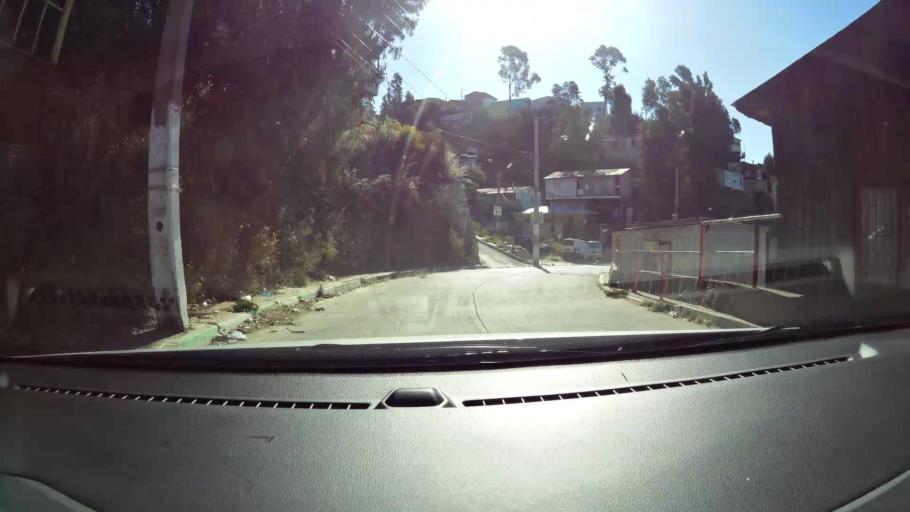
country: CL
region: Valparaiso
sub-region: Provincia de Valparaiso
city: Valparaiso
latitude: -33.0600
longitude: -71.6219
